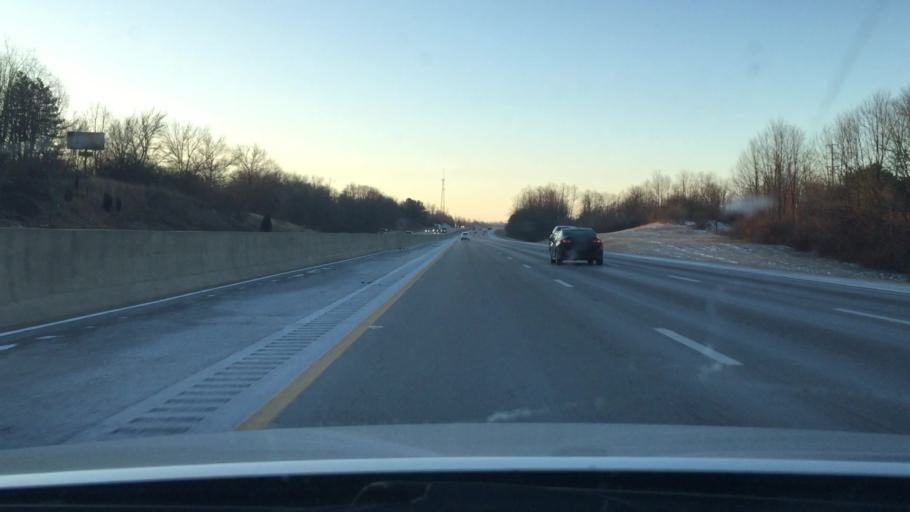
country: US
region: Kentucky
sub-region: Grant County
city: Crittenden
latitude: 38.7503
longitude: -84.6063
